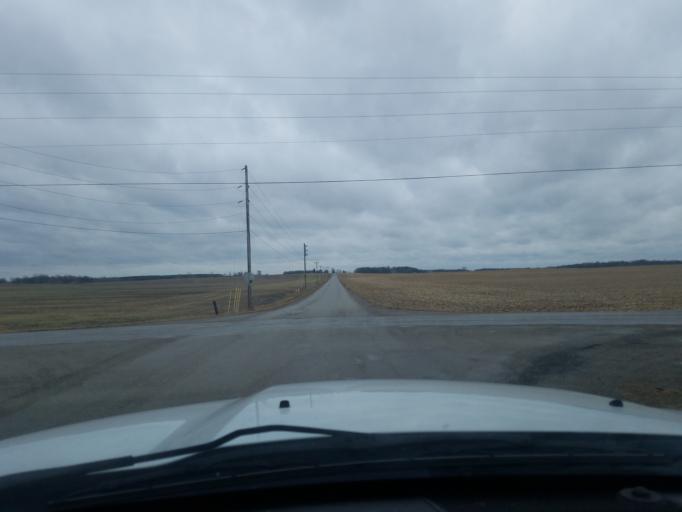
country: US
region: Indiana
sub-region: Noble County
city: Albion
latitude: 41.4386
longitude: -85.3946
